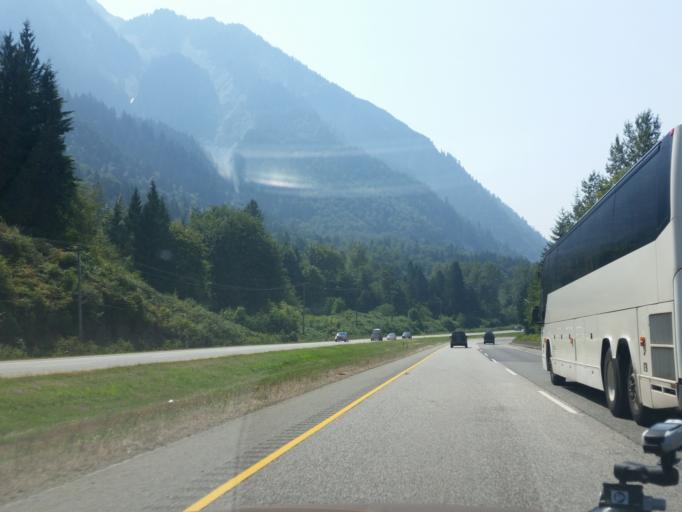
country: CA
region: British Columbia
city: Agassiz
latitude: 49.2190
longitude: -121.6912
